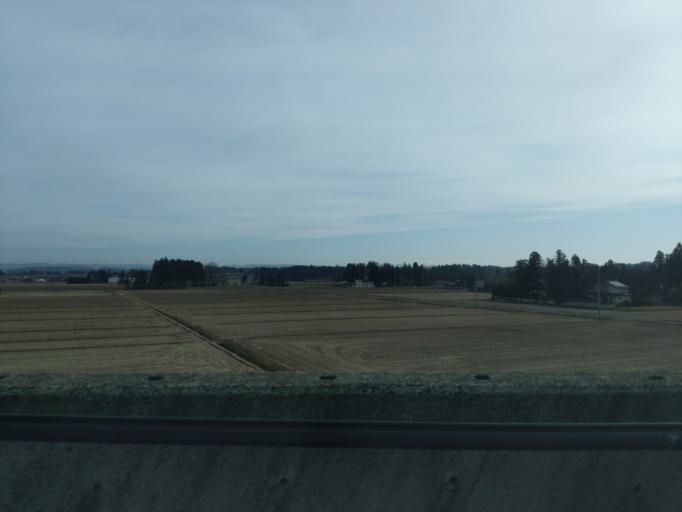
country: JP
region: Iwate
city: Ichinoseki
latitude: 38.7565
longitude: 141.0761
